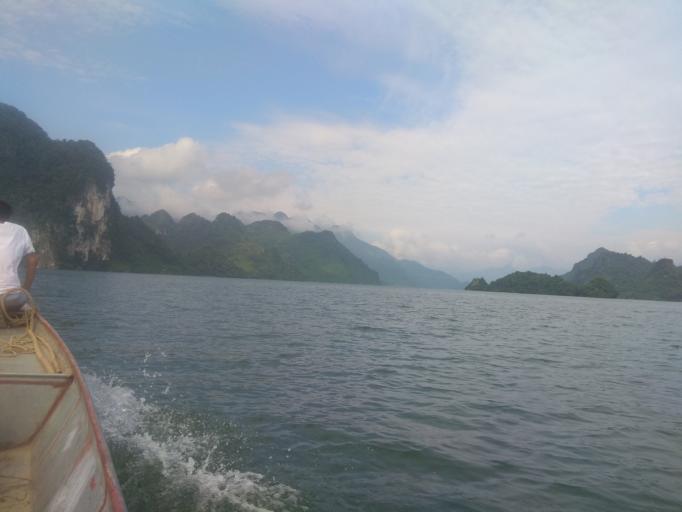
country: VN
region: Hoa Binh
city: Da Bac
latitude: 20.7517
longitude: 105.1444
